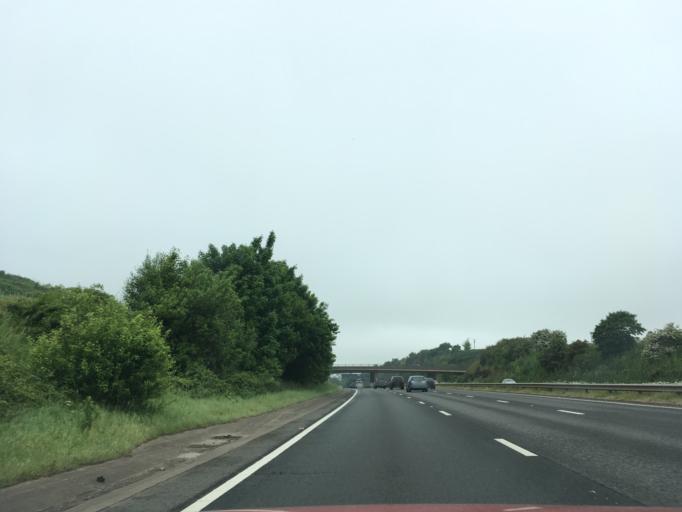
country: GB
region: England
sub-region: Devon
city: Exminster
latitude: 50.6757
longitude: -3.5308
